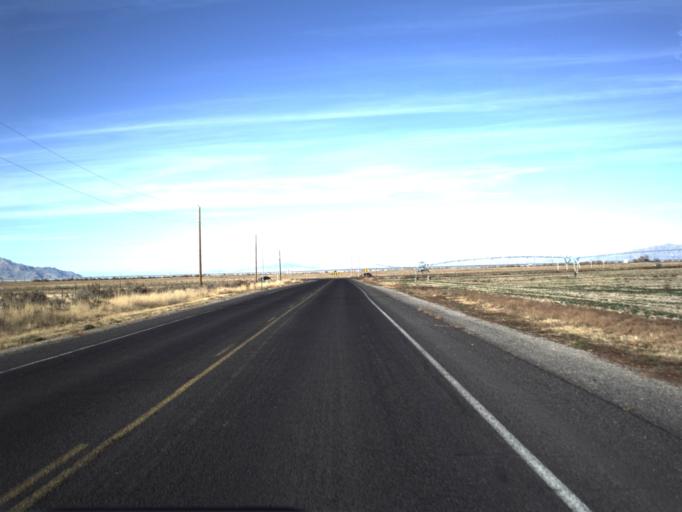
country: US
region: Utah
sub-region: Tooele County
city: Erda
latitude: 40.6113
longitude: -112.3709
